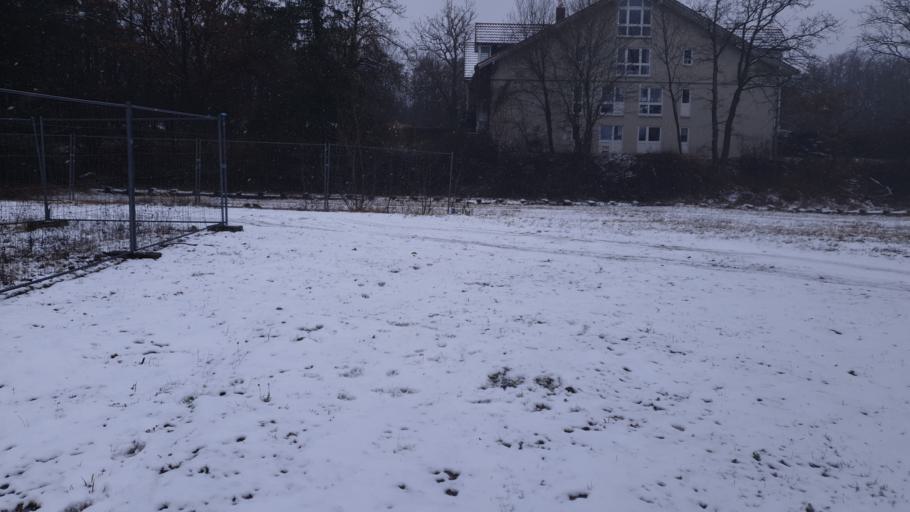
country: DE
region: Bavaria
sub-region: Upper Bavaria
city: Grafelfing
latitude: 48.1338
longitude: 11.4229
